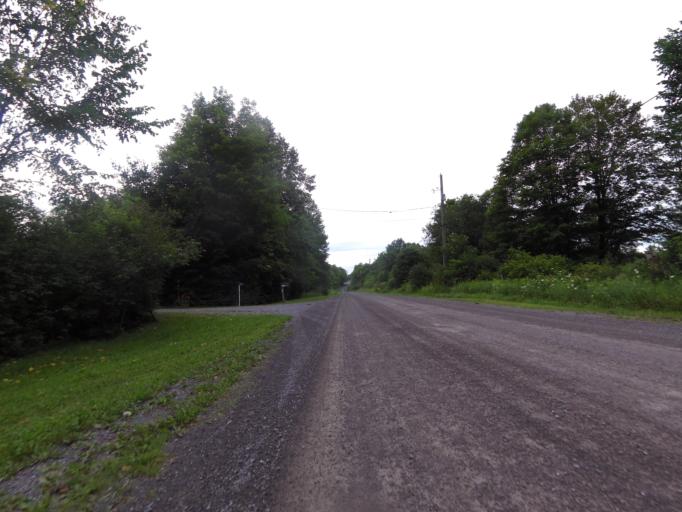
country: CA
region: Ontario
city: Carleton Place
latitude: 45.1665
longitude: -76.2763
